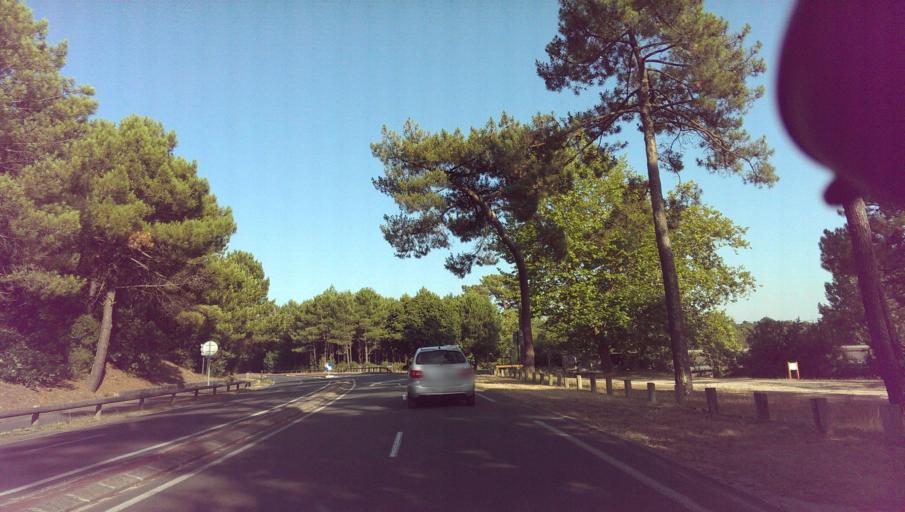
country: FR
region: Aquitaine
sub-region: Departement des Landes
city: Mimizan
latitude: 44.2107
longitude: -1.2748
